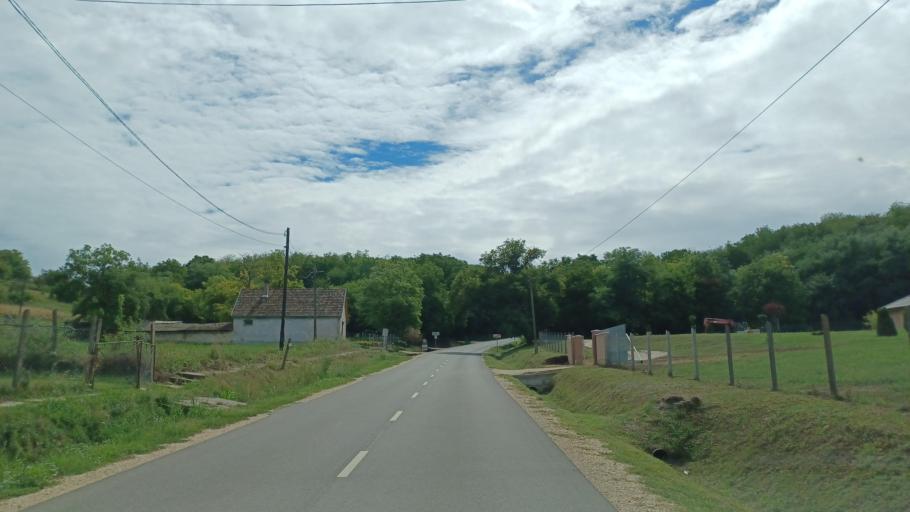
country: HU
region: Tolna
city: Zomba
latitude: 46.4975
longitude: 18.5919
